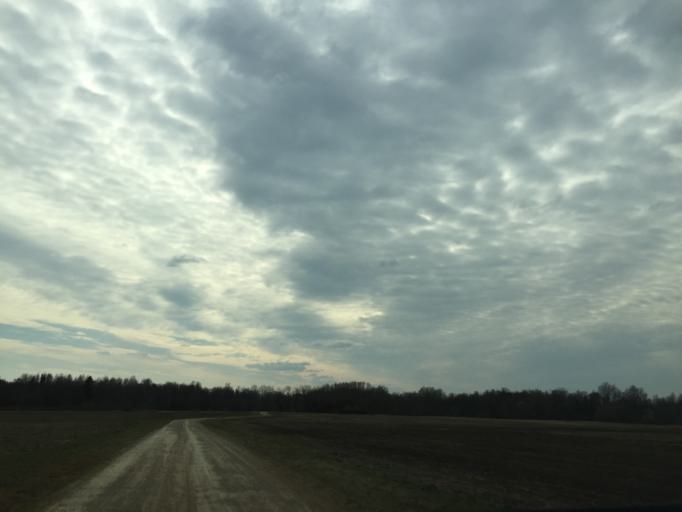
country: EE
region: Ida-Virumaa
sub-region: Sillamaee linn
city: Sillamae
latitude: 59.3880
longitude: 27.9012
